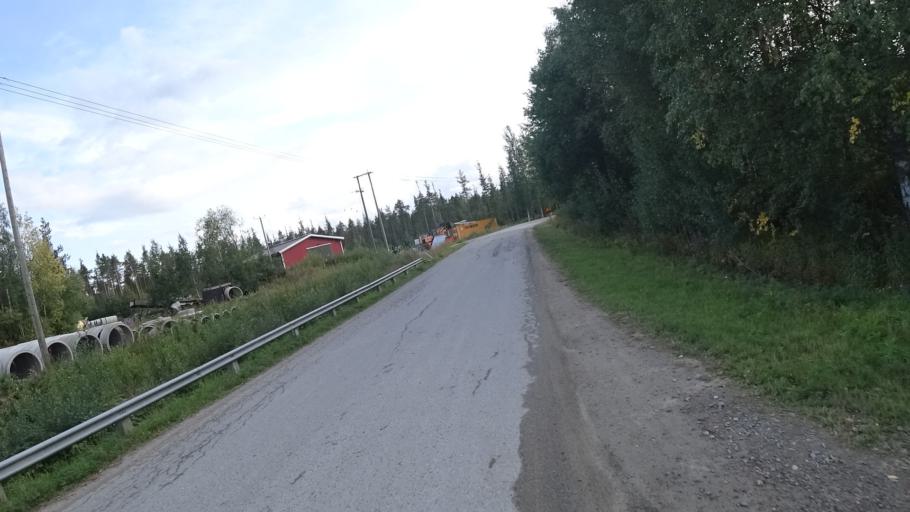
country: FI
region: North Karelia
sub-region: Joensuu
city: Ilomantsi
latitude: 62.6695
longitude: 30.9530
